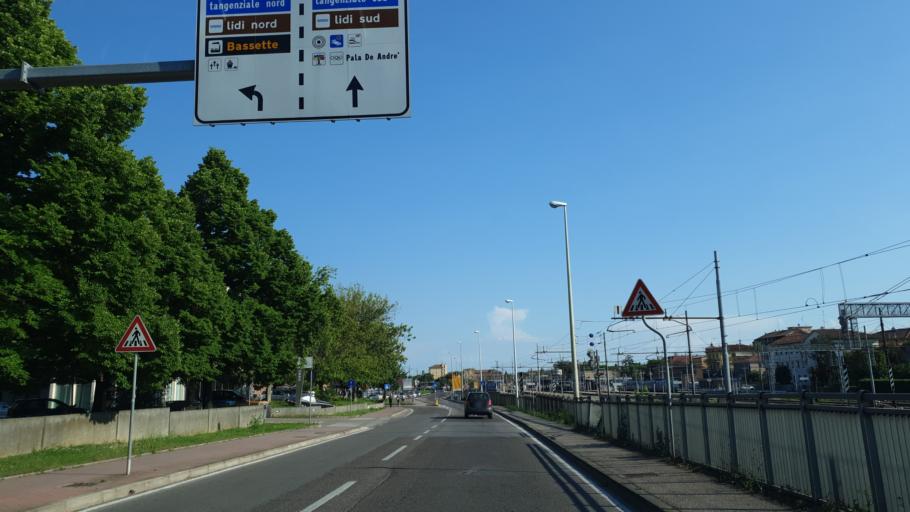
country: IT
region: Emilia-Romagna
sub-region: Provincia di Ravenna
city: Ravenna
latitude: 44.4225
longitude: 12.2079
